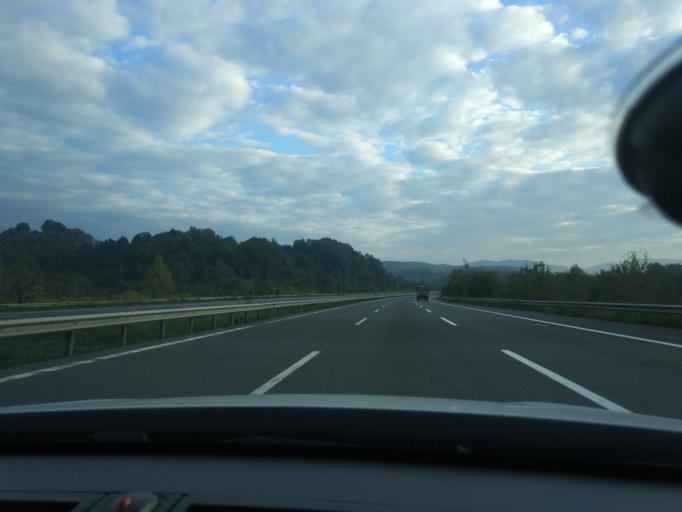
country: TR
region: Sakarya
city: Hendek
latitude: 40.7741
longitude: 30.7845
